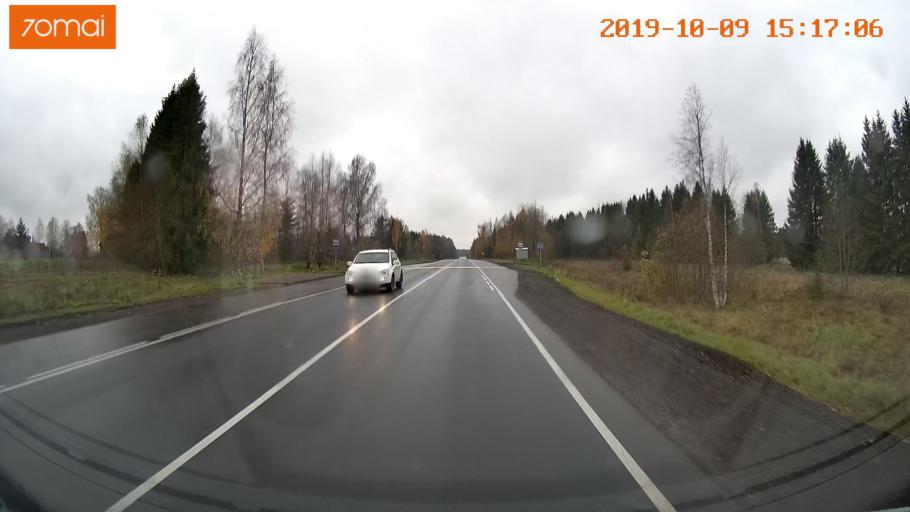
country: RU
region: Kostroma
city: Susanino
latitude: 58.1028
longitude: 41.5840
